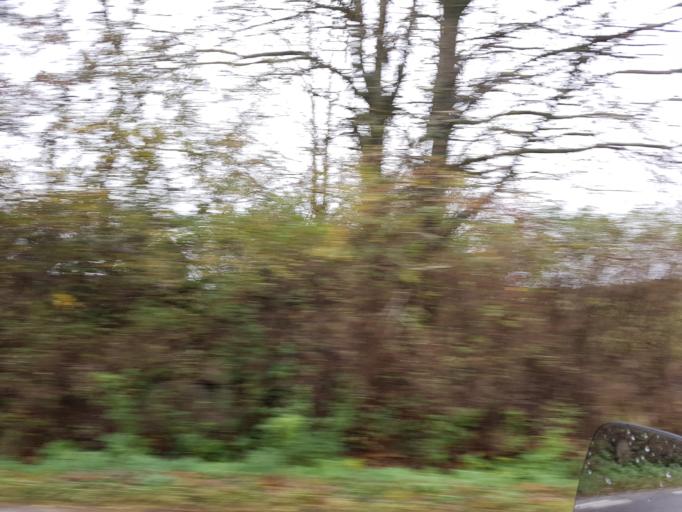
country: SE
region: Vaestra Goetaland
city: Svanesund
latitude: 58.1597
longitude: 11.7754
